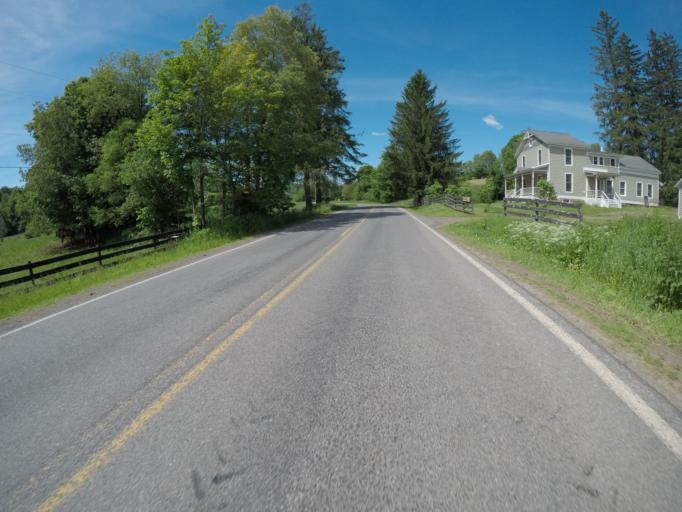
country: US
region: New York
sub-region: Delaware County
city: Delhi
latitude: 42.1677
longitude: -74.7886
